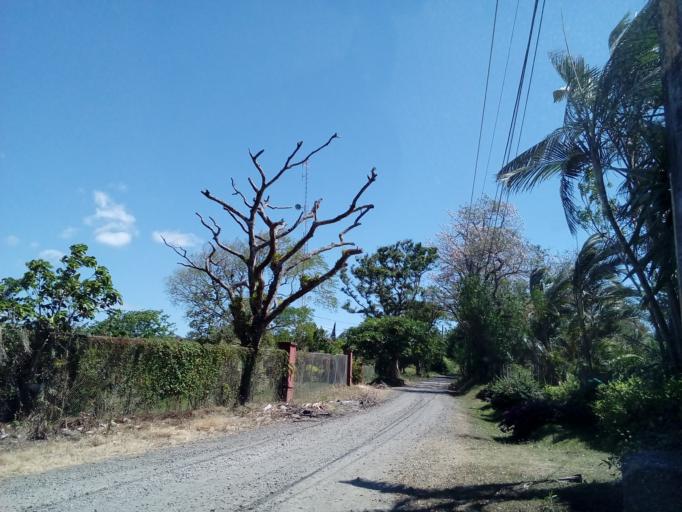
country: CR
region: Guanacaste
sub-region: Canton de Tilaran
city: Tilaran
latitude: 10.5076
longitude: -84.9371
